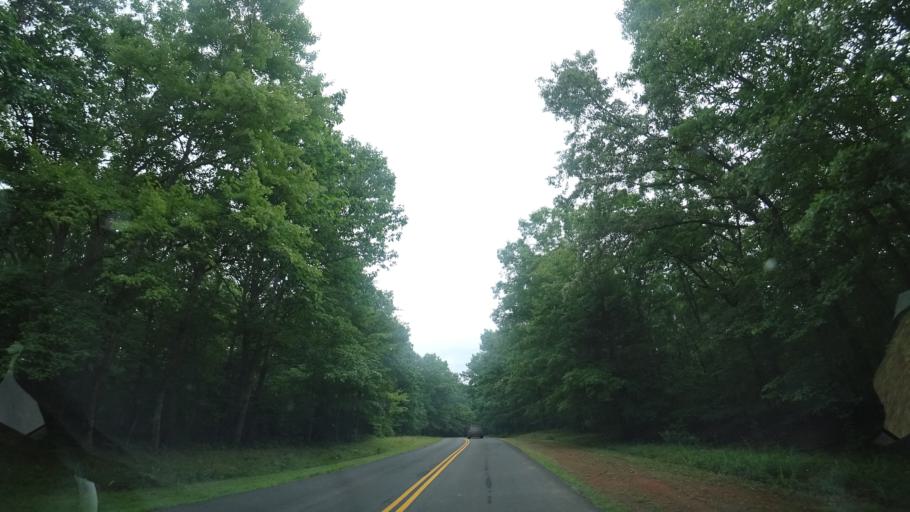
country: US
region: Virginia
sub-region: Louisa County
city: Louisa
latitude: 38.1318
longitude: -77.8188
